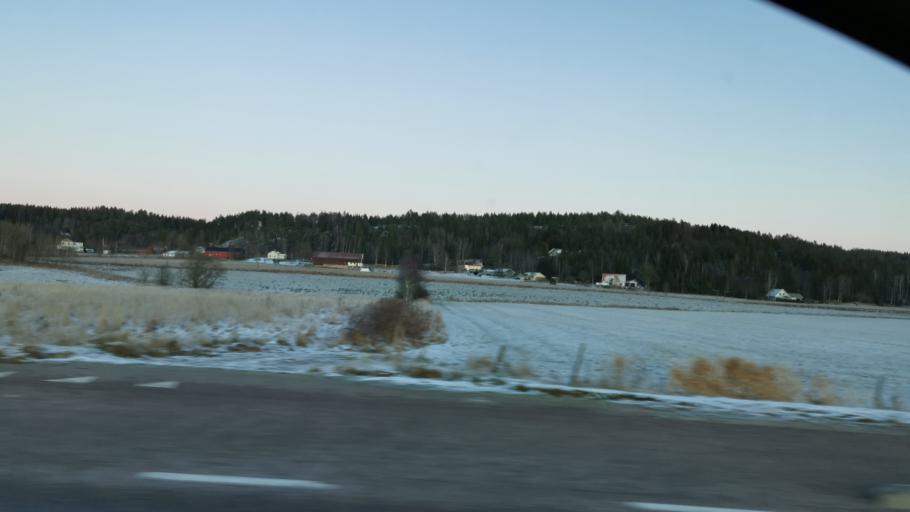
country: SE
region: Vaestra Goetaland
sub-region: Munkedals Kommun
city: Munkedal
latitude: 58.3921
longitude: 11.7605
